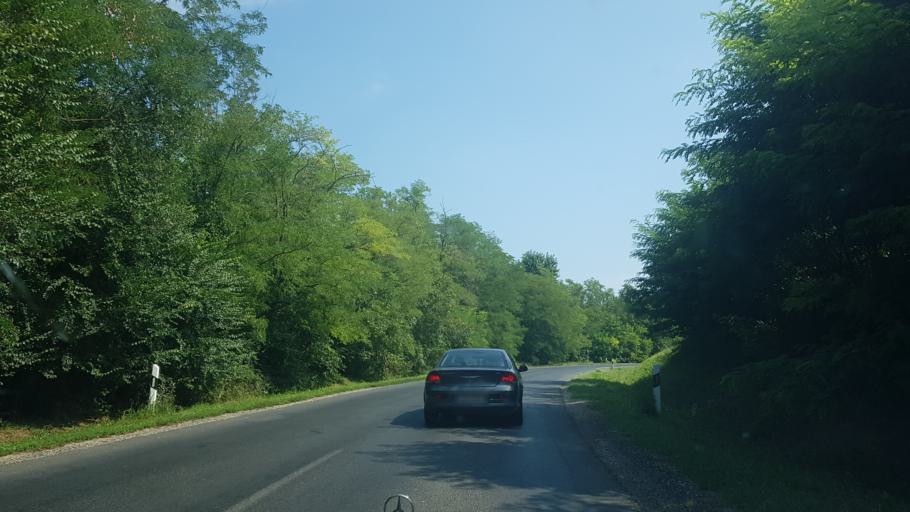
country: HU
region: Somogy
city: Bohonye
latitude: 46.4874
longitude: 17.4091
